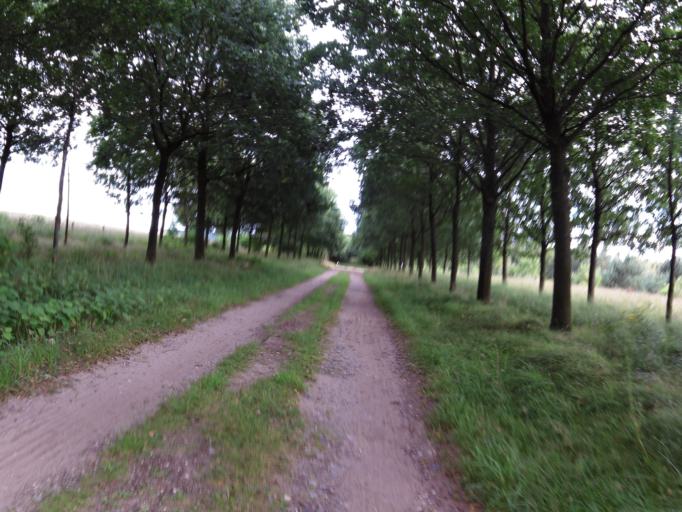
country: NL
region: Gelderland
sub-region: Gemeente Arnhem
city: Gulden Bodem
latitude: 52.0531
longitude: 5.9136
